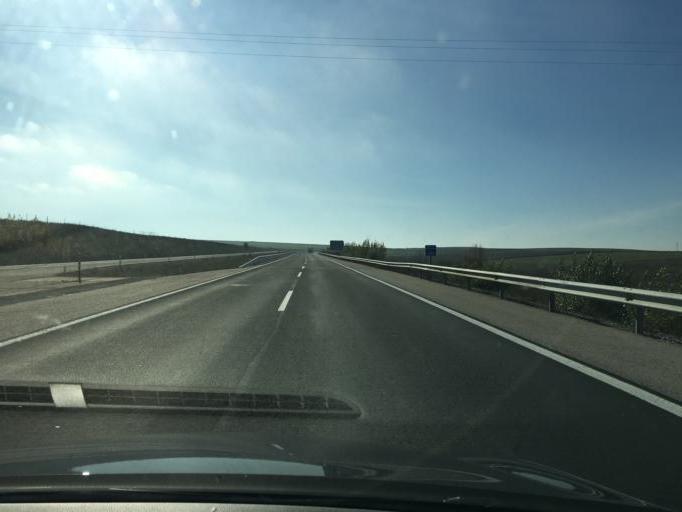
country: ES
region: Castille and Leon
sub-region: Provincia de Burgos
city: Zuneda
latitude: 42.5982
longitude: -3.2261
